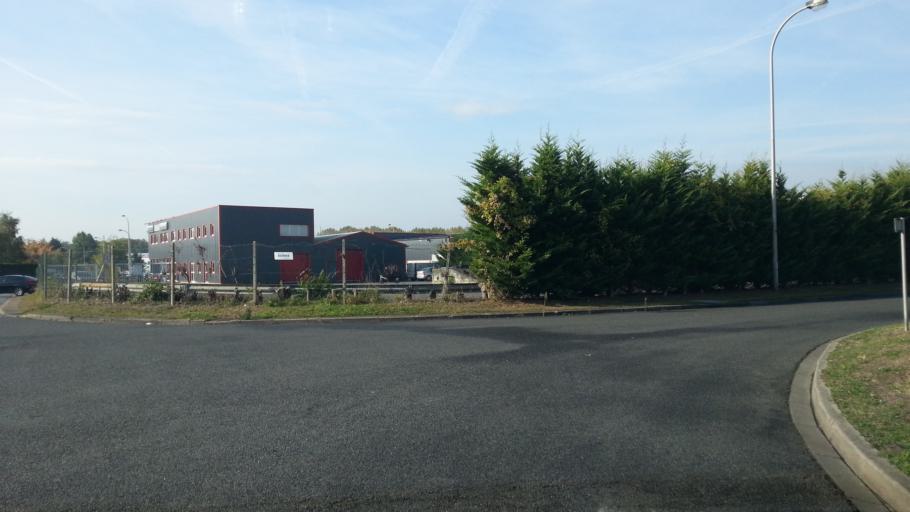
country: FR
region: Picardie
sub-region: Departement de l'Oise
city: Saint-Maximin
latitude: 49.2401
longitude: 2.4632
